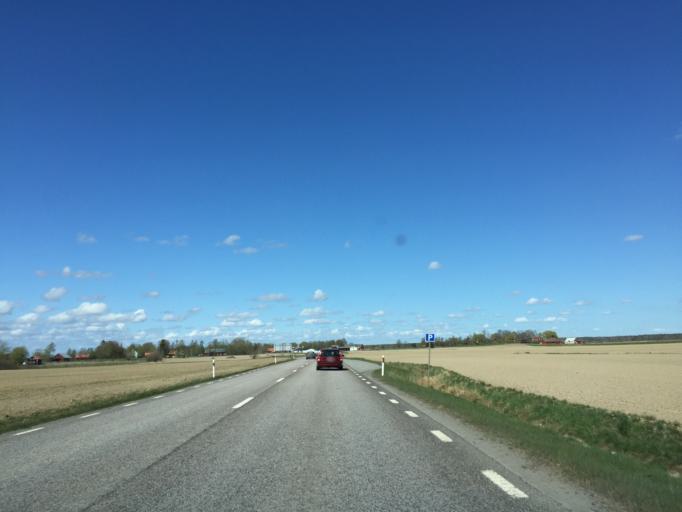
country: SE
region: OErebro
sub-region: Kumla Kommun
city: Hallabrottet
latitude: 59.1692
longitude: 15.2628
